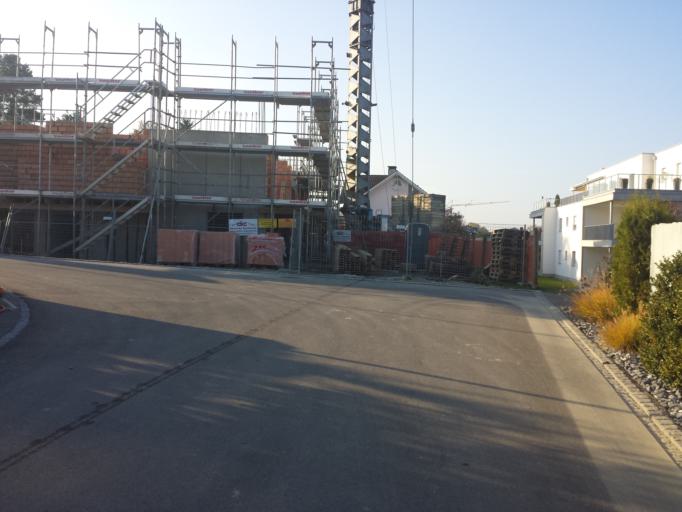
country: CH
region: Thurgau
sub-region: Arbon District
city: Romanshorn
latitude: 47.5724
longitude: 9.3740
